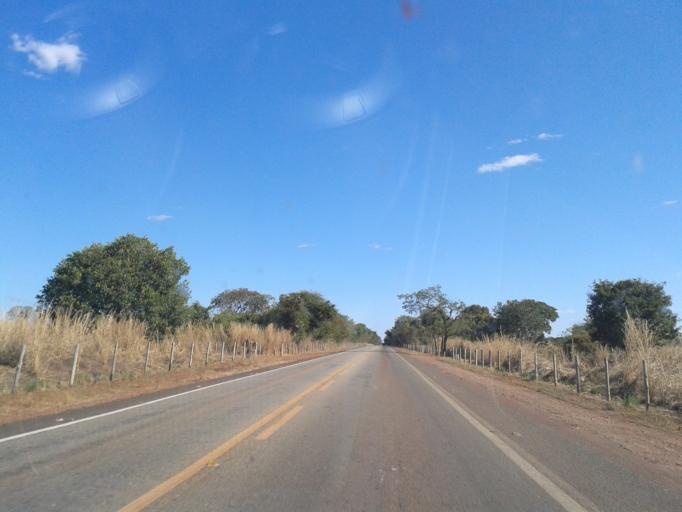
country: BR
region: Goias
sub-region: Mozarlandia
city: Mozarlandia
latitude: -14.6645
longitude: -50.5317
